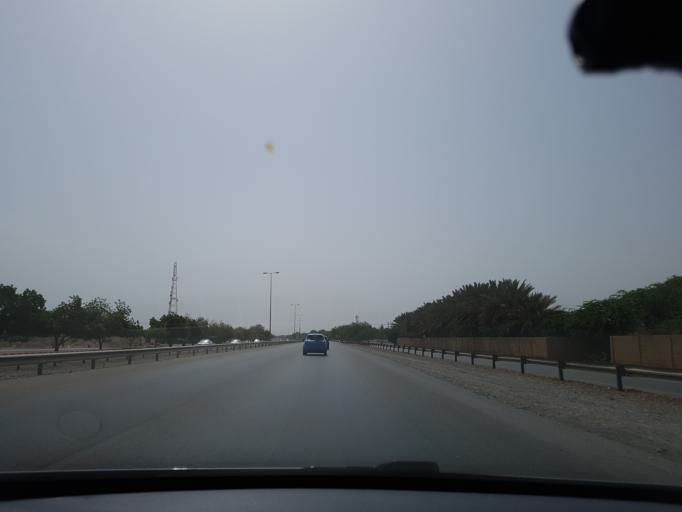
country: OM
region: Al Batinah
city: As Suwayq
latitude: 23.8444
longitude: 57.3642
